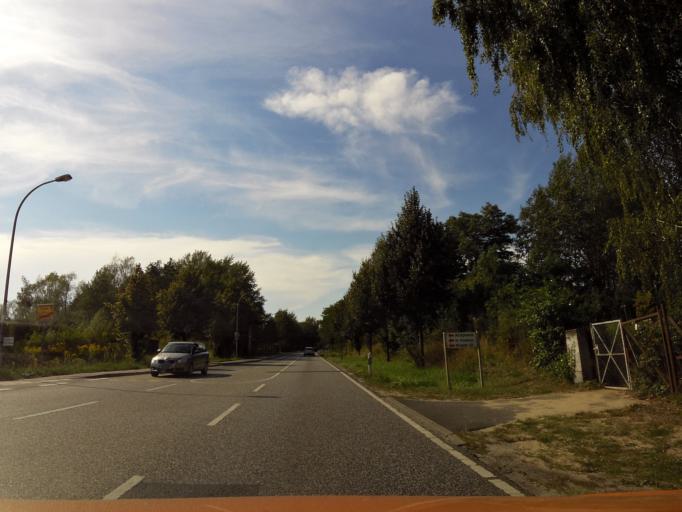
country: DE
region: Brandenburg
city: Teltow
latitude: 52.3778
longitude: 13.2585
